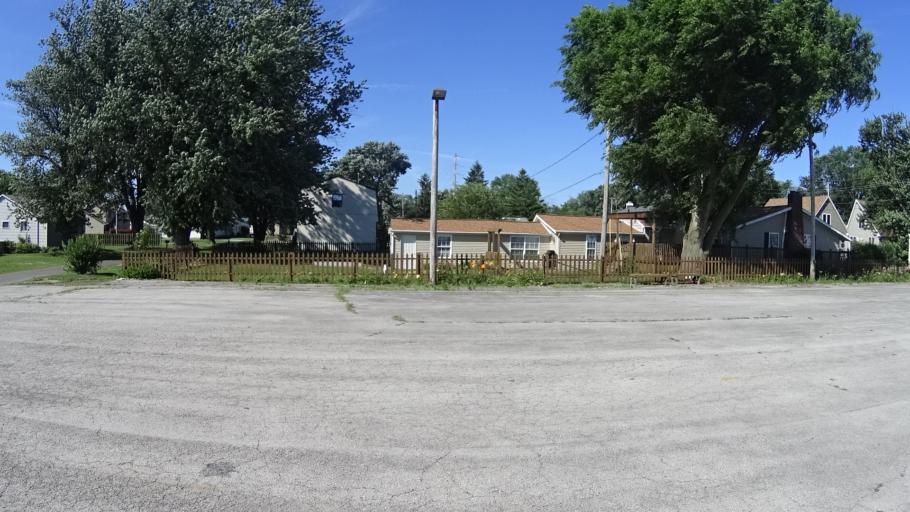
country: US
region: Ohio
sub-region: Ottawa County
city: Port Clinton
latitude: 41.4729
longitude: -82.8259
